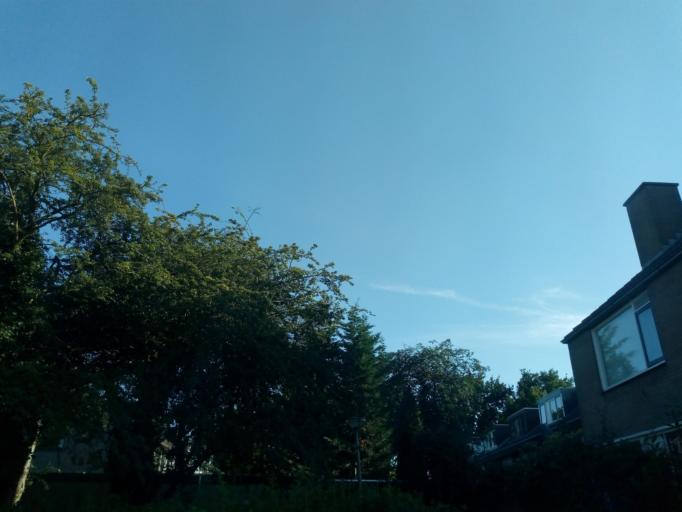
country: NL
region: South Holland
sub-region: Gemeente Alphen aan den Rijn
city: Alphen aan den Rijn
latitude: 52.1444
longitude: 4.6530
